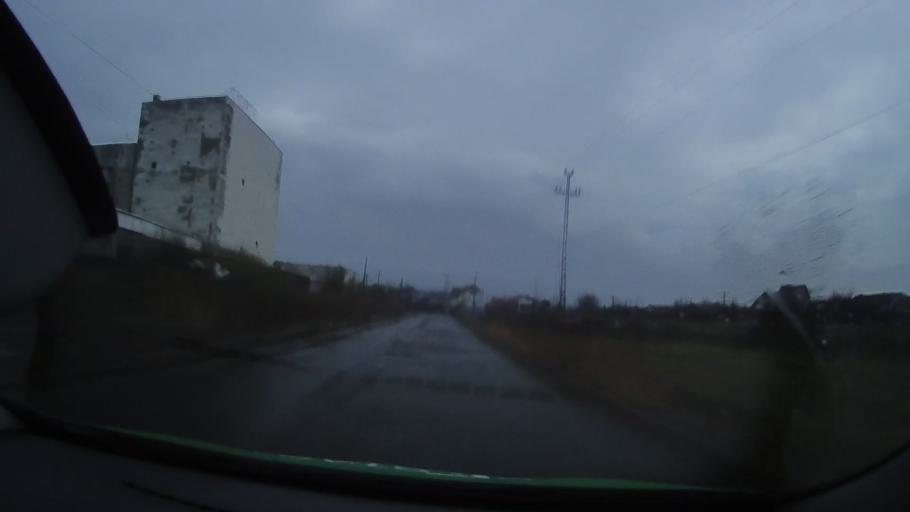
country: RO
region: Mures
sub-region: Municipiul Reghin
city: Iernuteni
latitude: 46.7676
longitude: 24.7223
